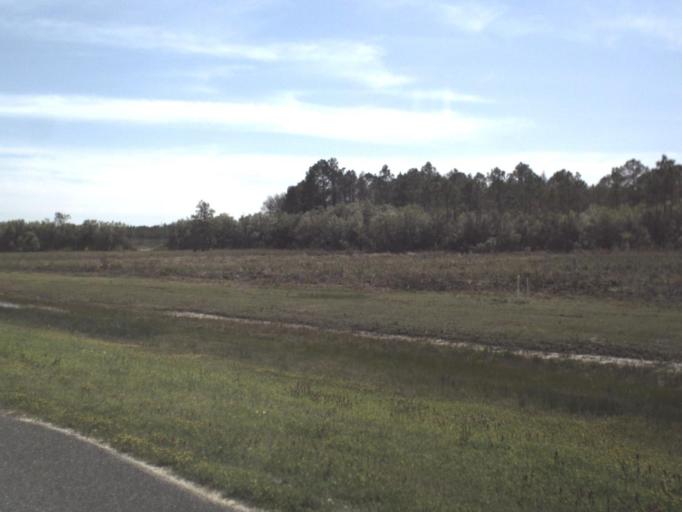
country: US
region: Florida
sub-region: Bay County
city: Lynn Haven
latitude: 30.3593
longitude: -85.6692
